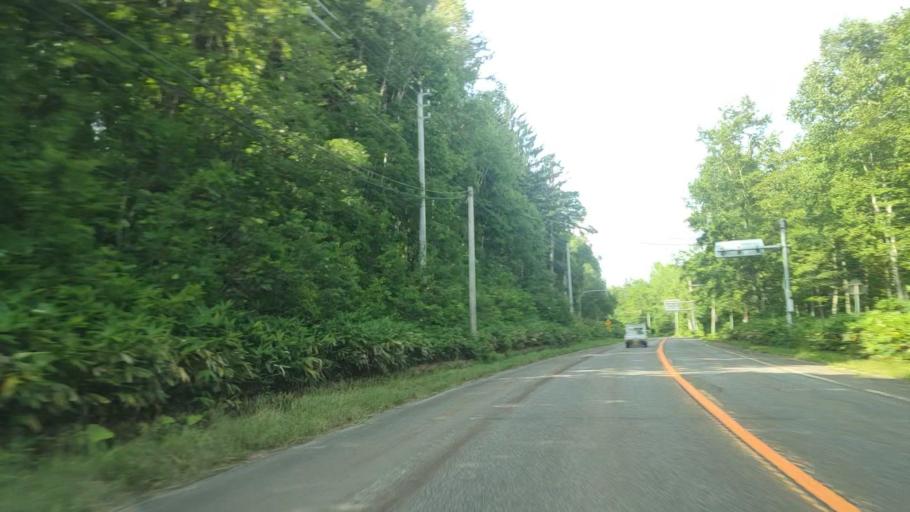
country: JP
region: Hokkaido
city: Nayoro
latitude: 44.3877
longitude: 142.3977
